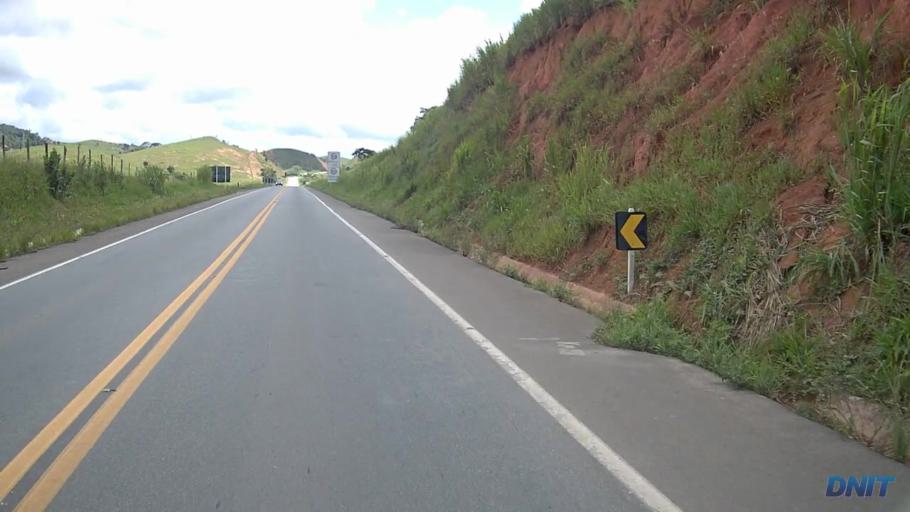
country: BR
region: Minas Gerais
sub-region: Belo Oriente
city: Belo Oriente
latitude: -19.1345
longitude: -42.2132
